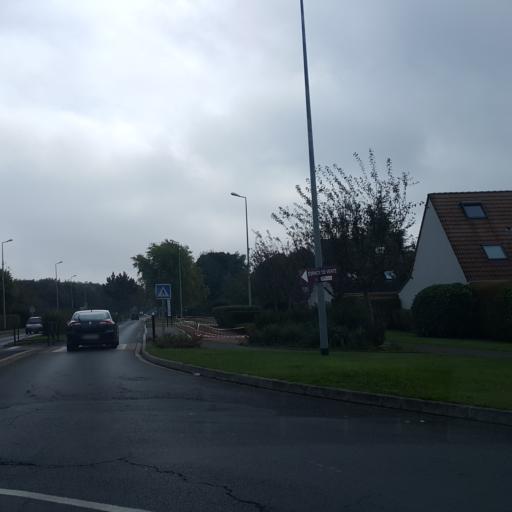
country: FR
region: Ile-de-France
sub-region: Departement de l'Essonne
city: Saint-Pierre-du-Perray
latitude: 48.6181
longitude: 2.4964
